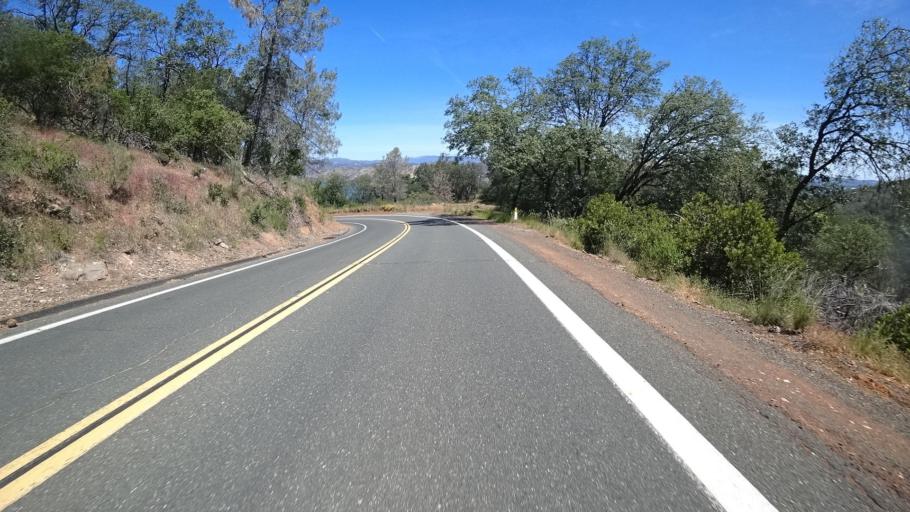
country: US
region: California
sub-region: Lake County
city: Clearlake
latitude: 38.9404
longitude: -122.6687
